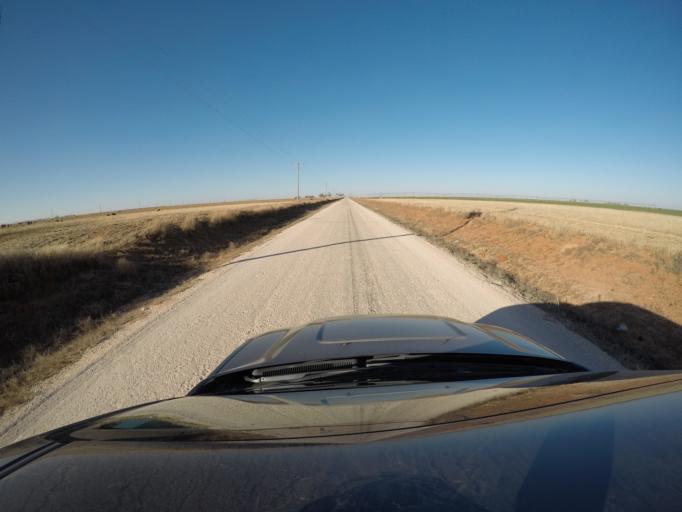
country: US
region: New Mexico
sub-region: Curry County
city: Texico
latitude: 34.3401
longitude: -103.1083
